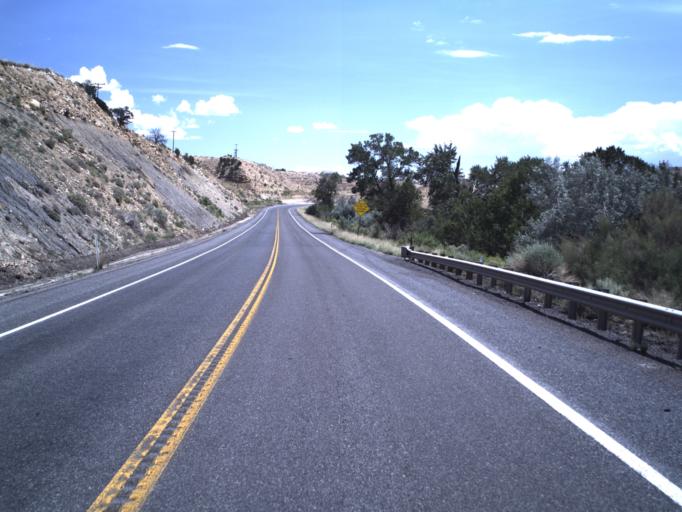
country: US
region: Utah
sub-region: Emery County
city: Huntington
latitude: 39.3762
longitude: -111.0679
